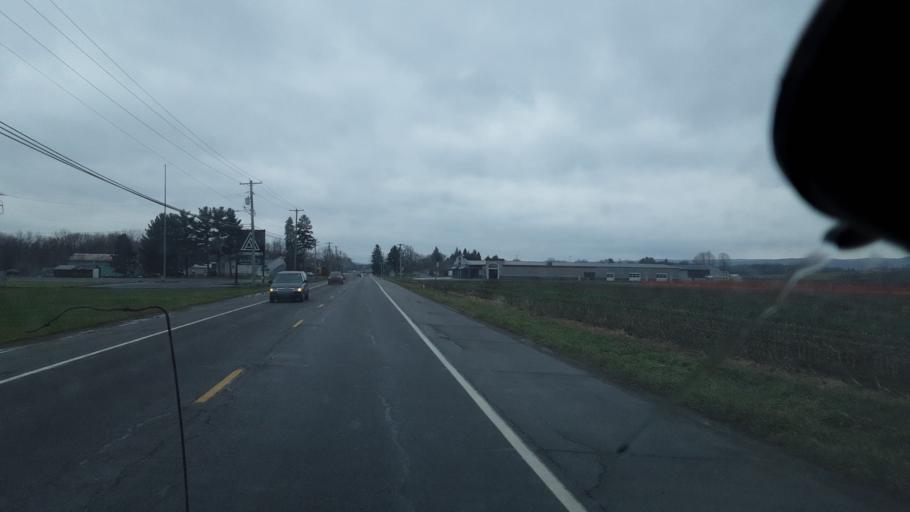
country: US
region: New York
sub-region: Cattaraugus County
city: Yorkshire
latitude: 42.5491
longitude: -78.4782
